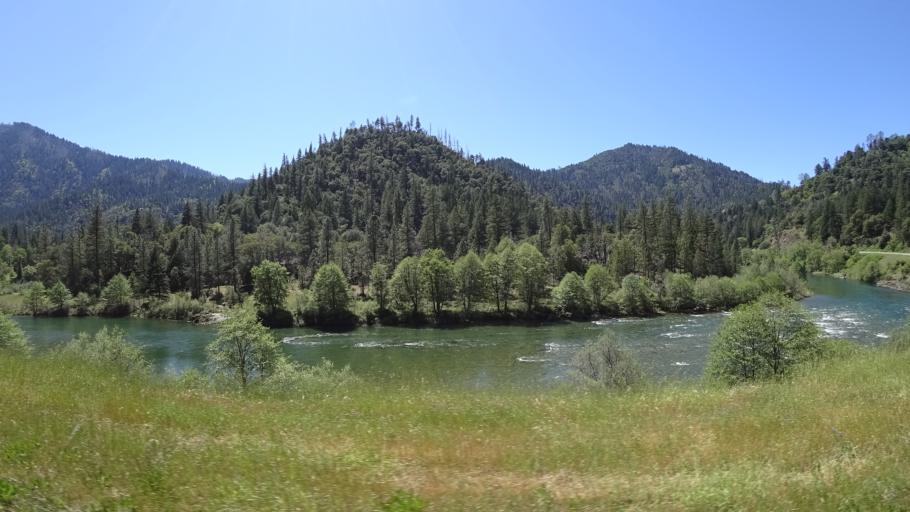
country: US
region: California
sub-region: Trinity County
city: Hayfork
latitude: 40.7837
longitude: -123.3354
